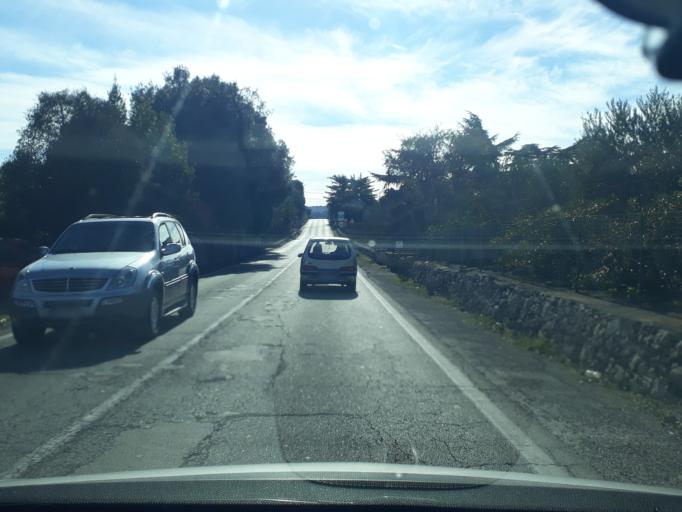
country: IT
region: Apulia
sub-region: Provincia di Bari
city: Locorotondo
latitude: 40.7321
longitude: 17.3326
